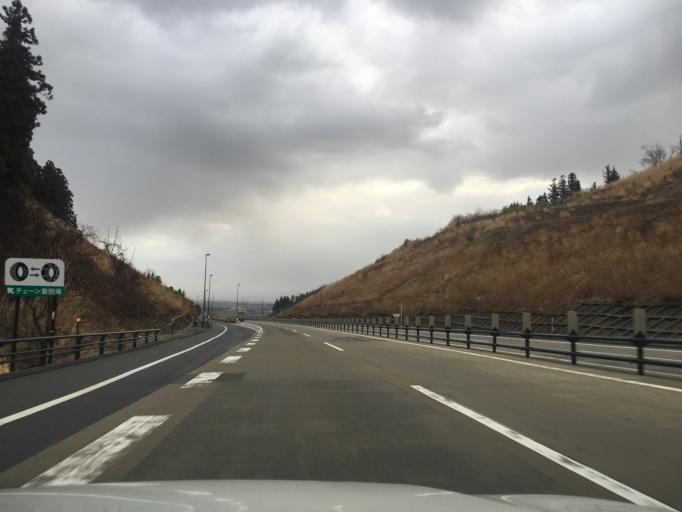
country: JP
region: Yamagata
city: Tsuruoka
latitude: 38.7000
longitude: 139.7167
